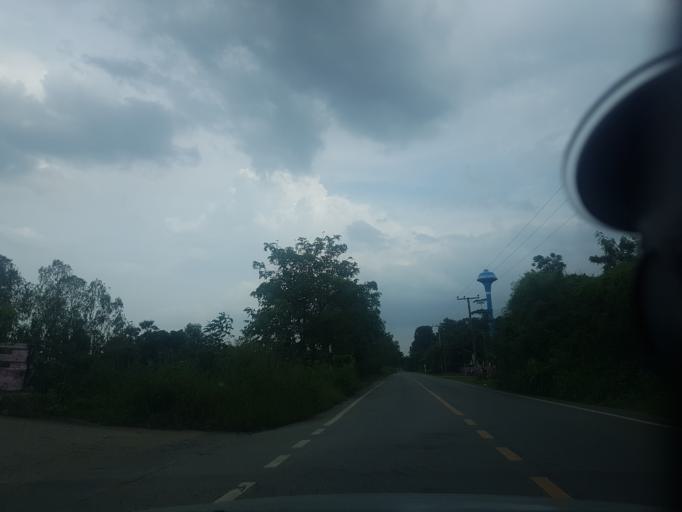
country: TH
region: Pathum Thani
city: Nong Suea
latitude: 14.1075
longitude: 100.8685
